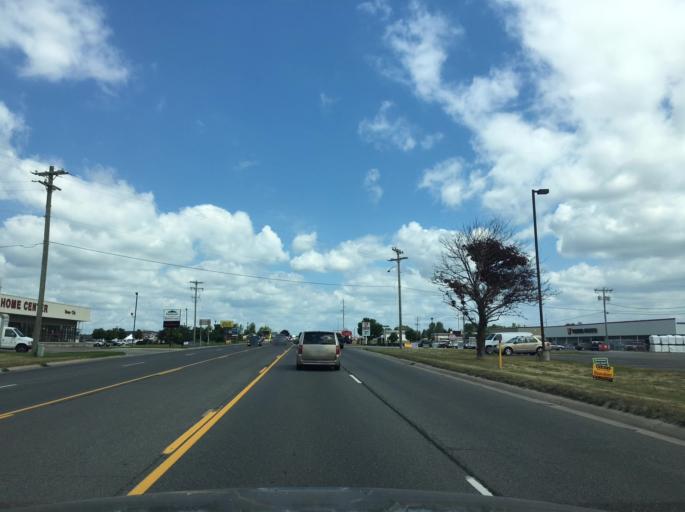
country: US
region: Michigan
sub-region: Grand Traverse County
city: Traverse City
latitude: 44.6760
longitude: -85.6563
